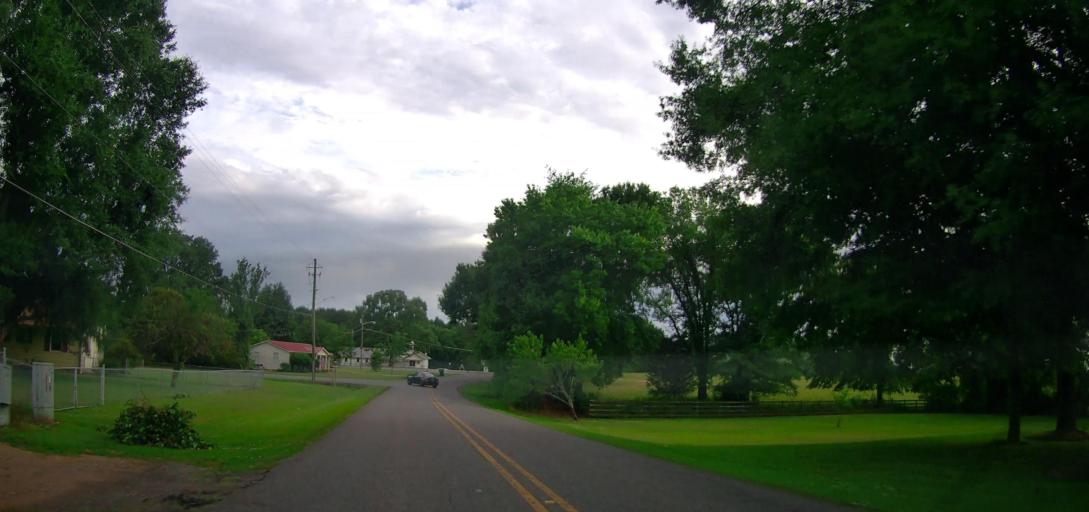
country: US
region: Alabama
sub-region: Calhoun County
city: Oxford
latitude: 33.5818
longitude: -85.8296
